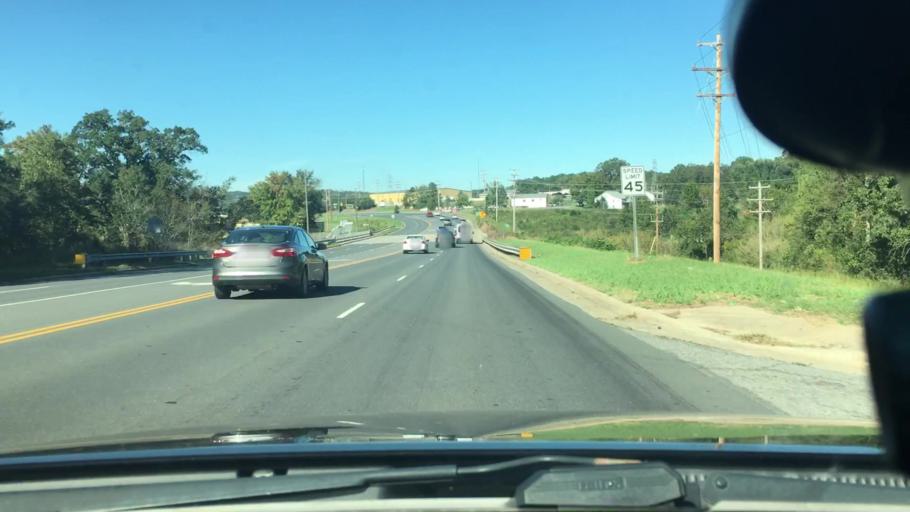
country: US
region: North Carolina
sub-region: Stanly County
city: Albemarle
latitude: 35.3394
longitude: -80.2088
